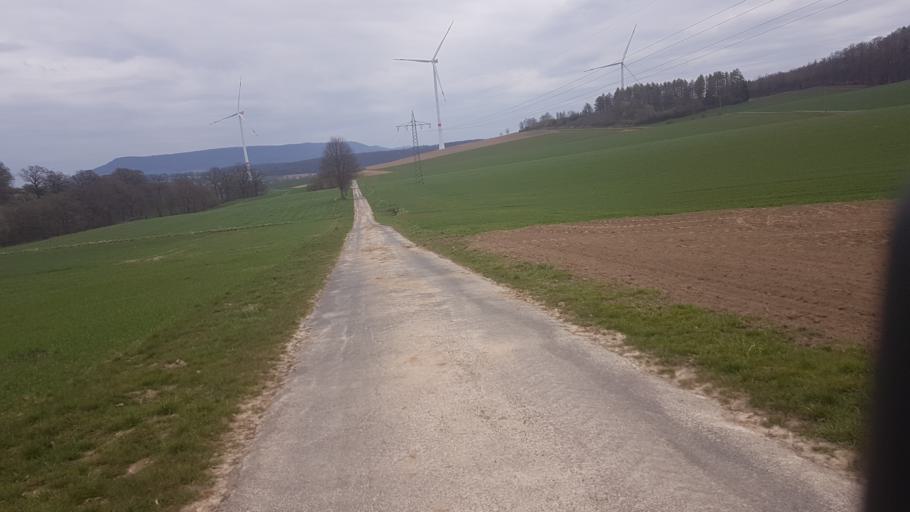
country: DE
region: Lower Saxony
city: Hameln
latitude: 52.1410
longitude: 9.4162
